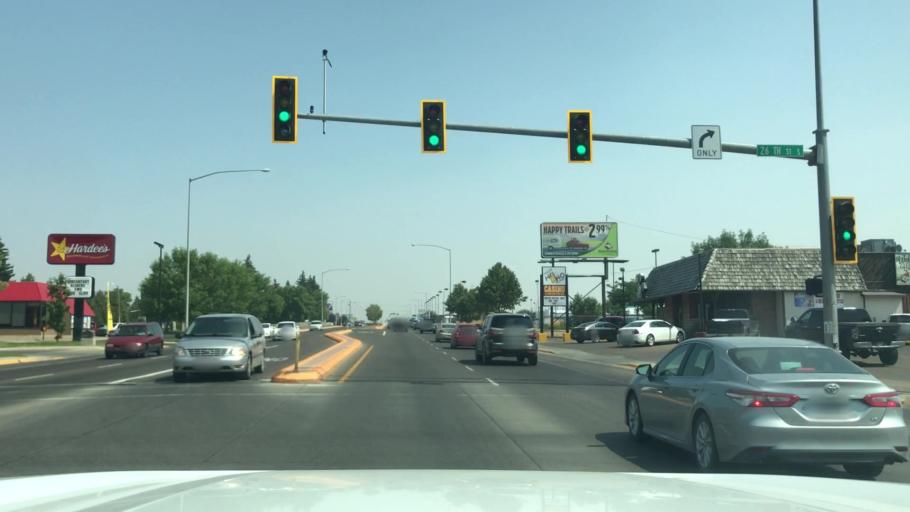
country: US
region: Montana
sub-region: Cascade County
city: Great Falls
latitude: 47.4941
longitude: -111.2627
